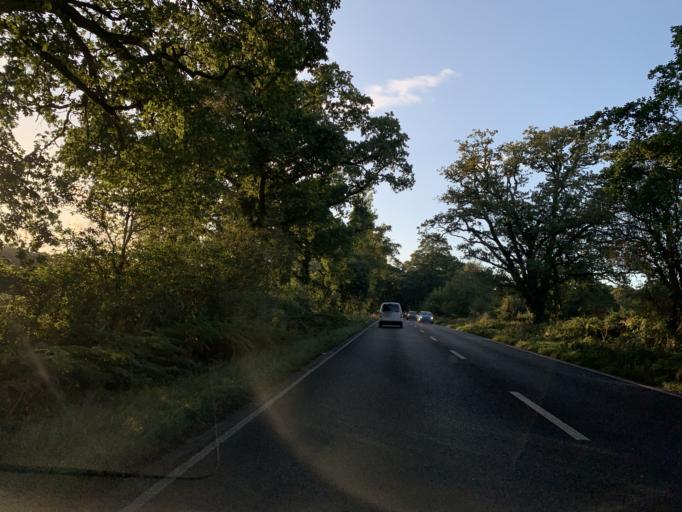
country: GB
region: England
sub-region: Hampshire
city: West Wellow
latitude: 50.9578
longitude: -1.5499
